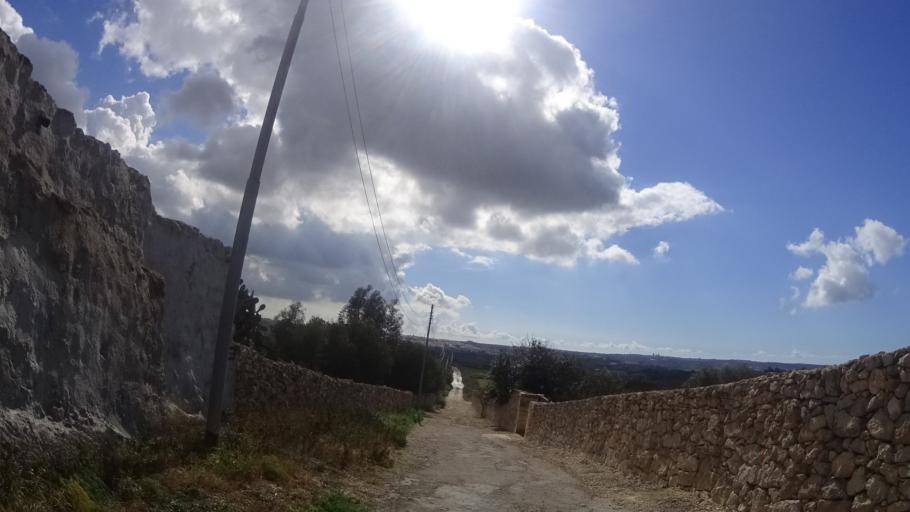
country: MT
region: L-Imtarfa
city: Imtarfa
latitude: 35.9055
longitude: 14.3841
